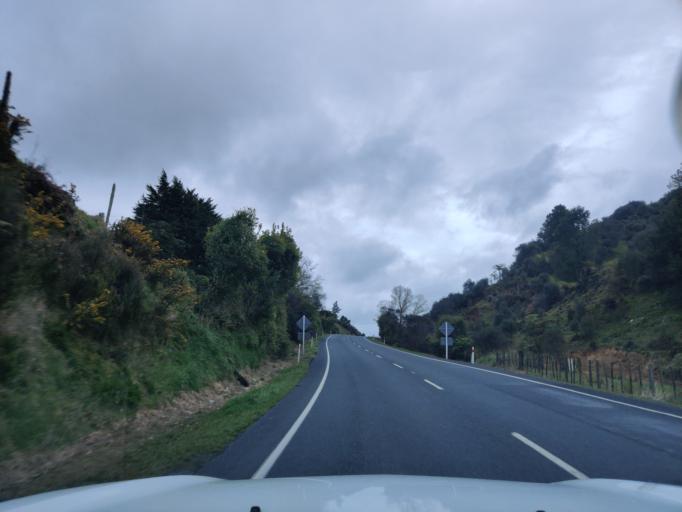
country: NZ
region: Waikato
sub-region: Otorohanga District
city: Otorohanga
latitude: -38.5131
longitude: 175.2085
